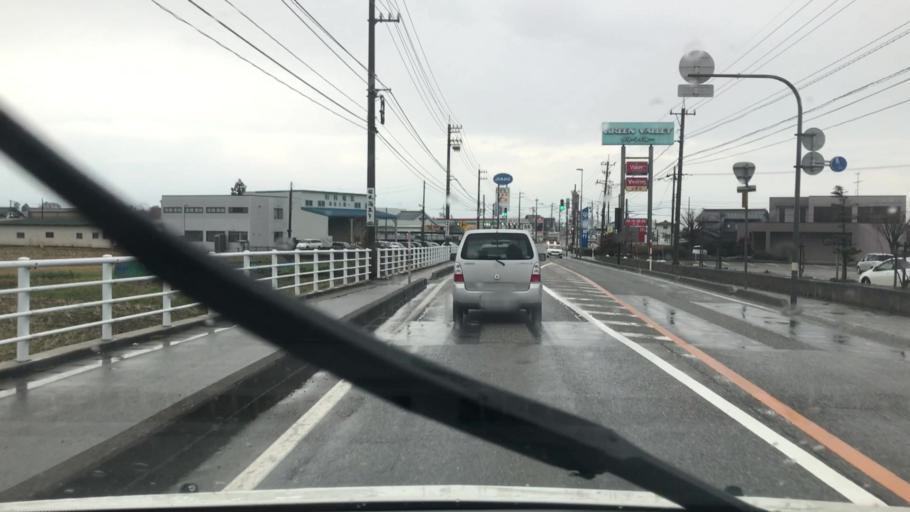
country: JP
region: Toyama
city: Yatsuomachi-higashikumisaka
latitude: 36.5931
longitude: 137.2042
